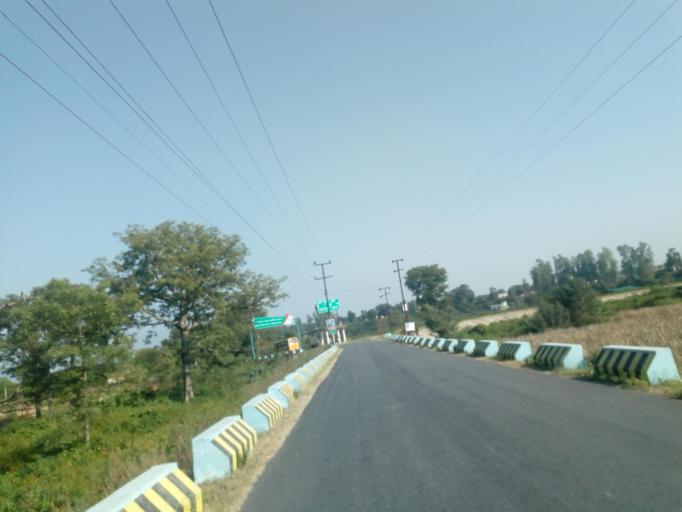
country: IN
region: Himachal Pradesh
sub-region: Sirmaur
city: Paonta Sahib
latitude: 30.4418
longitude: 77.6763
